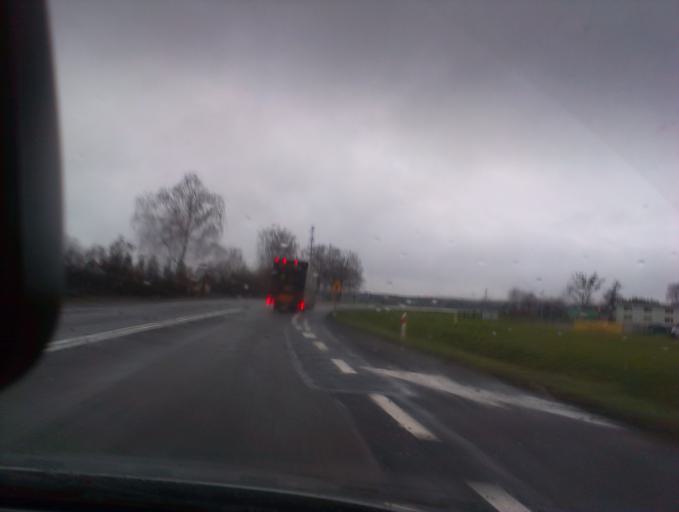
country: PL
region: Greater Poland Voivodeship
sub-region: Powiat chodzieski
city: Chodziez
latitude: 52.9502
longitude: 16.9421
